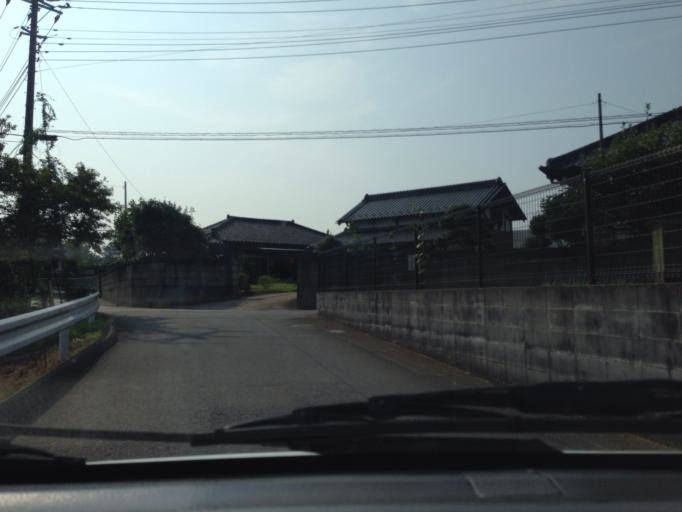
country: JP
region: Ibaraki
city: Ami
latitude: 36.0432
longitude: 140.2094
